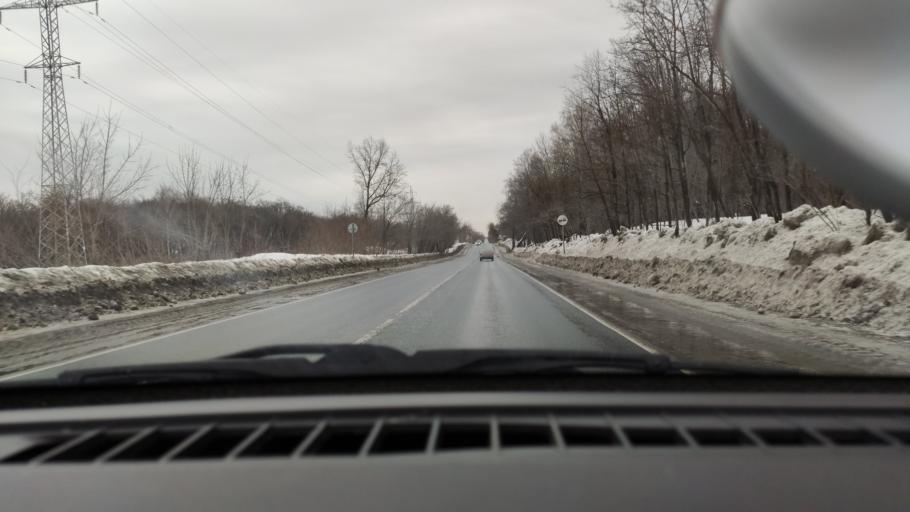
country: RU
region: Samara
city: Petra-Dubrava
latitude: 53.3165
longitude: 50.2701
